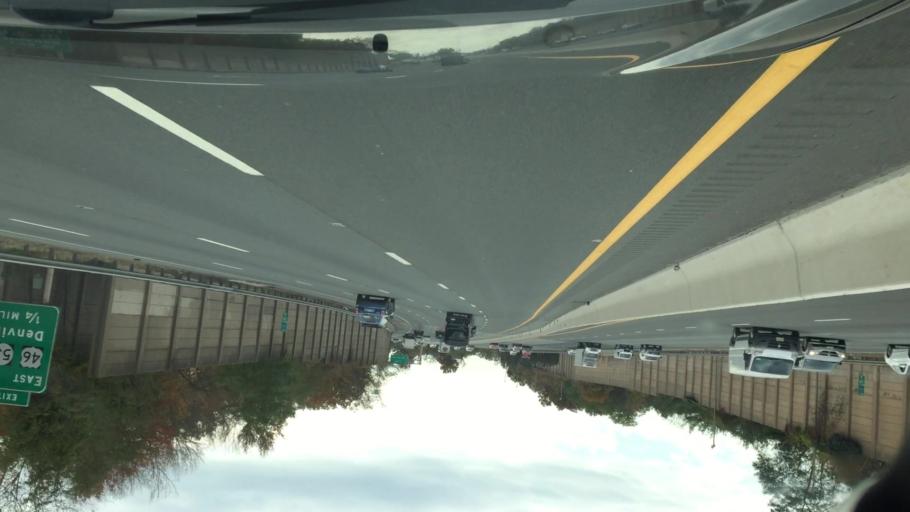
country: US
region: New Jersey
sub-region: Morris County
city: Rockaway
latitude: 40.9005
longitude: -74.4907
